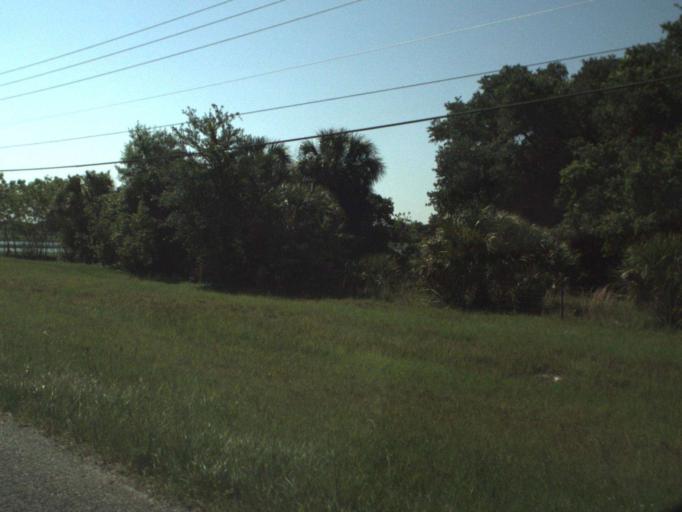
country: US
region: Florida
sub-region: Brevard County
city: Cocoa West
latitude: 28.3643
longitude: -80.8438
